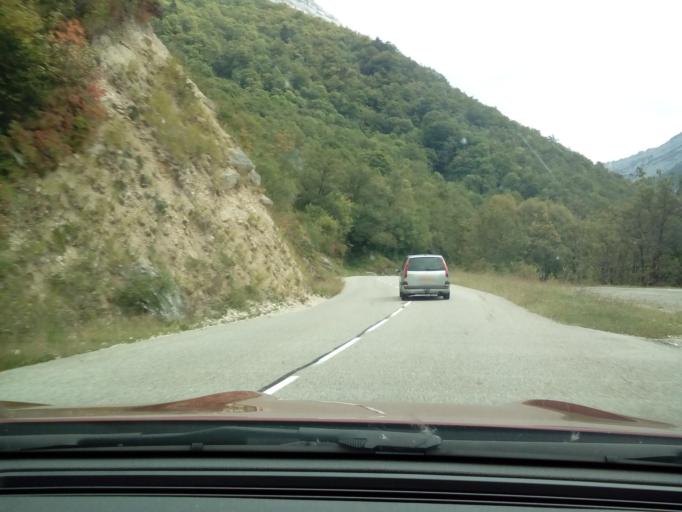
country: FR
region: Rhone-Alpes
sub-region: Departement de l'Isere
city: Pont-en-Royans
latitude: 45.0224
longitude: 5.3960
